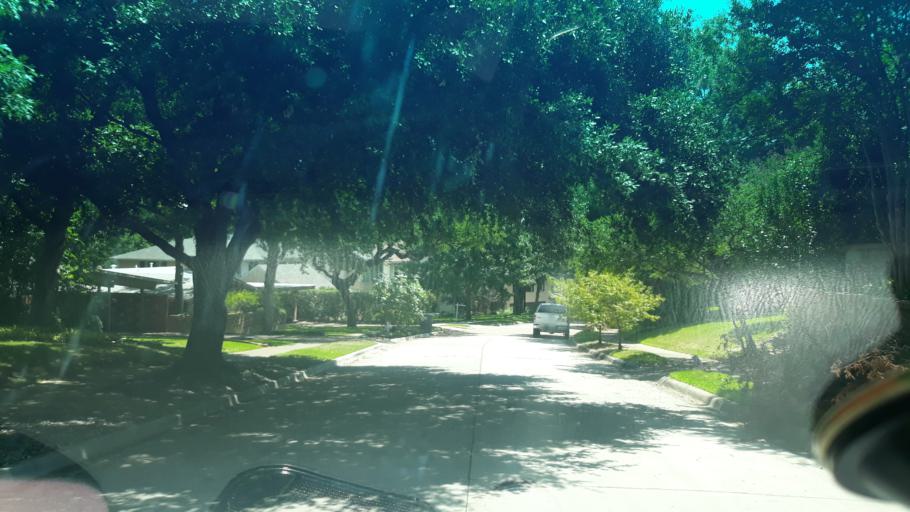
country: US
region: Texas
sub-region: Dallas County
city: Highland Park
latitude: 32.8155
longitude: -96.7352
